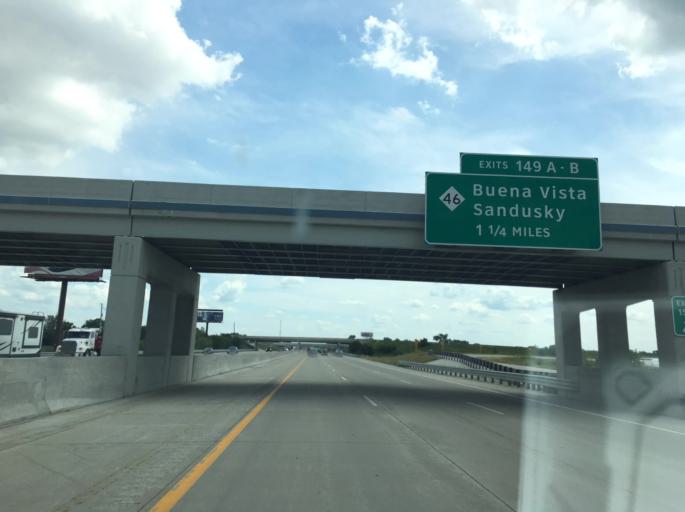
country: US
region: Michigan
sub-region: Saginaw County
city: Buena Vista
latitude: 43.4366
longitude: -83.8909
